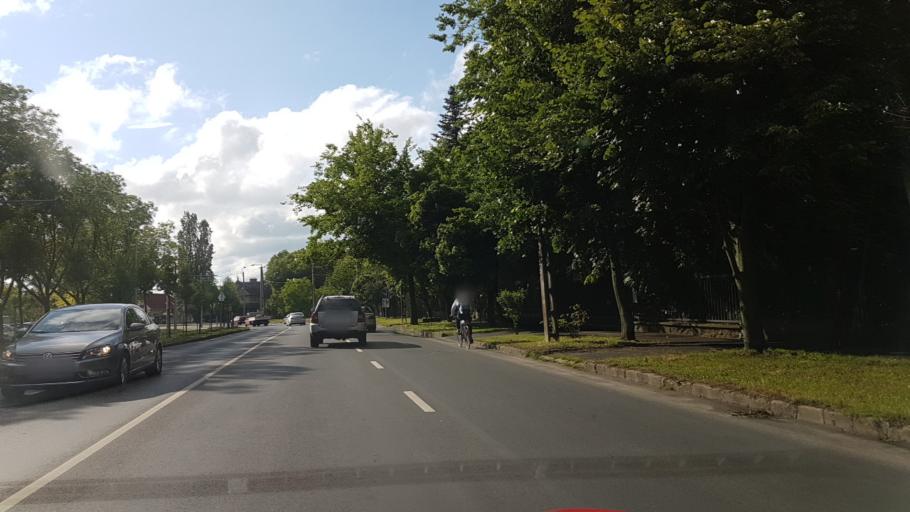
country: HU
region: Hajdu-Bihar
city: Debrecen
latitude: 47.5569
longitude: 21.6134
